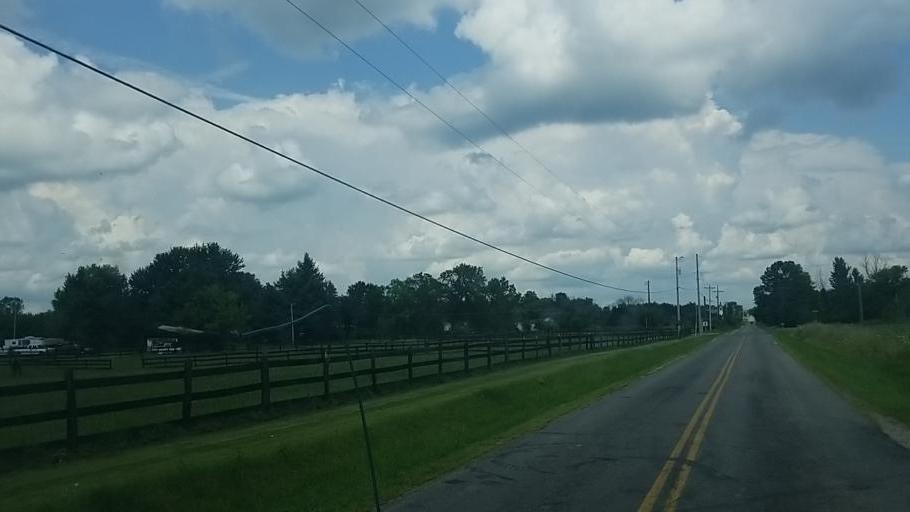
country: US
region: Ohio
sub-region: Medina County
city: Lodi
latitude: 41.0435
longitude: -82.0771
